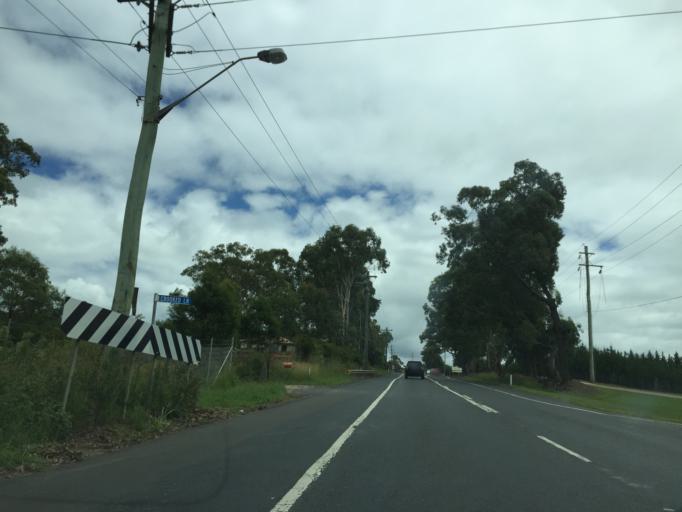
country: AU
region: New South Wales
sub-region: Hawkesbury
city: Richmond
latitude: -33.5748
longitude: 150.7143
